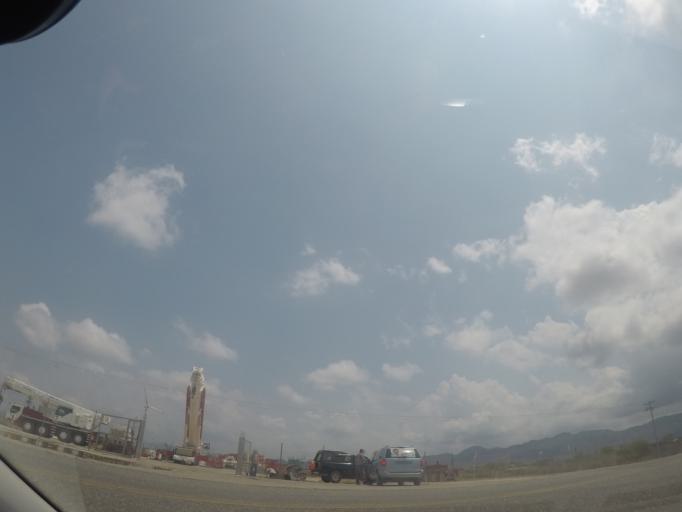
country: MX
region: Oaxaca
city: El Espinal
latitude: 16.5479
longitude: -94.9499
